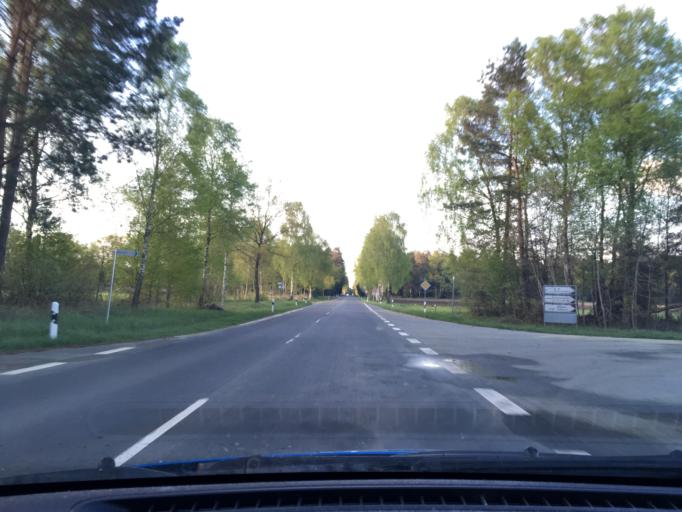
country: DE
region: Lower Saxony
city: Wietzendorf
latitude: 52.9656
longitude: 9.9781
